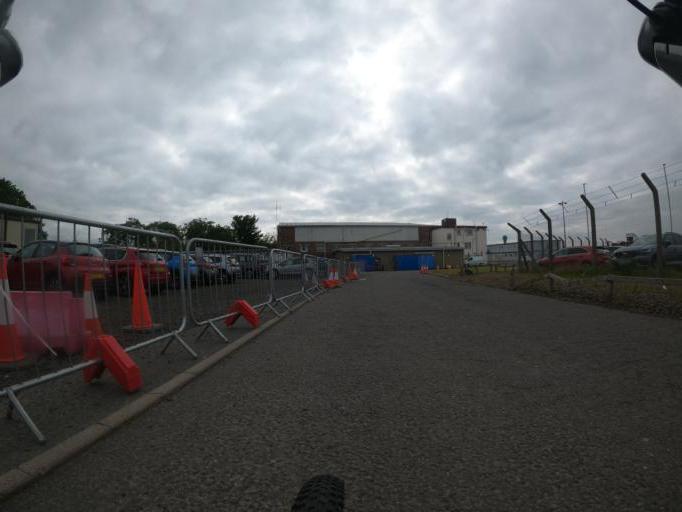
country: GB
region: Scotland
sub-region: Edinburgh
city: Ratho
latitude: 55.9440
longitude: -3.3509
